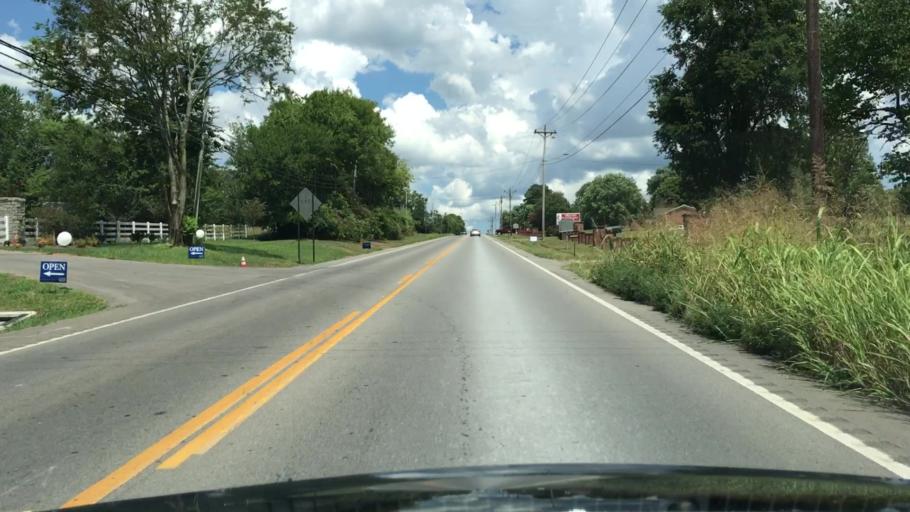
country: US
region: Tennessee
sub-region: Williamson County
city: Nolensville
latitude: 35.8633
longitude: -86.6589
